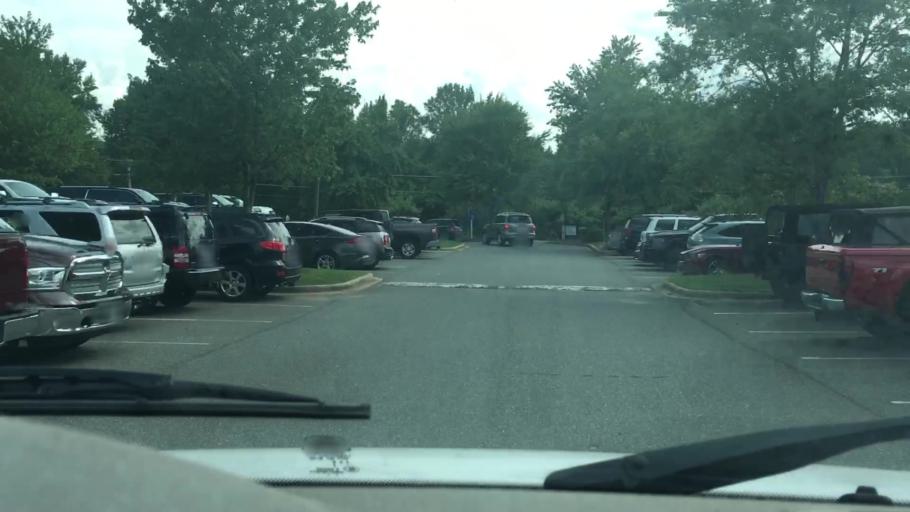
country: US
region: North Carolina
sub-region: Lincoln County
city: Lowesville
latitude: 35.4294
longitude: -80.9371
